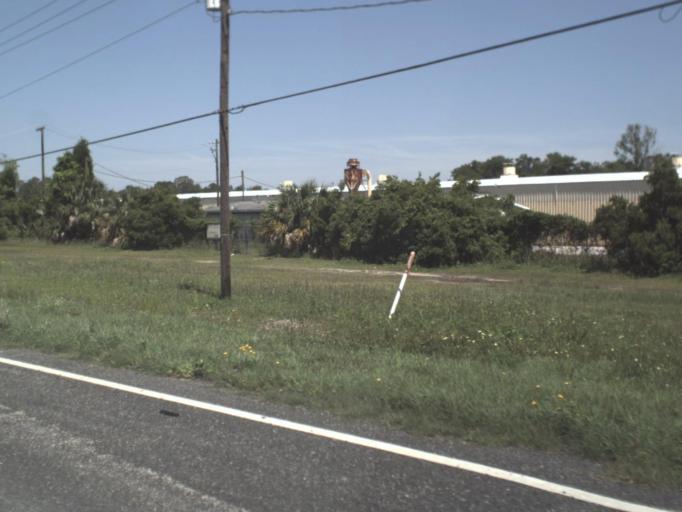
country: US
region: Florida
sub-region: Columbia County
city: Watertown
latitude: 30.1886
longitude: -82.5757
